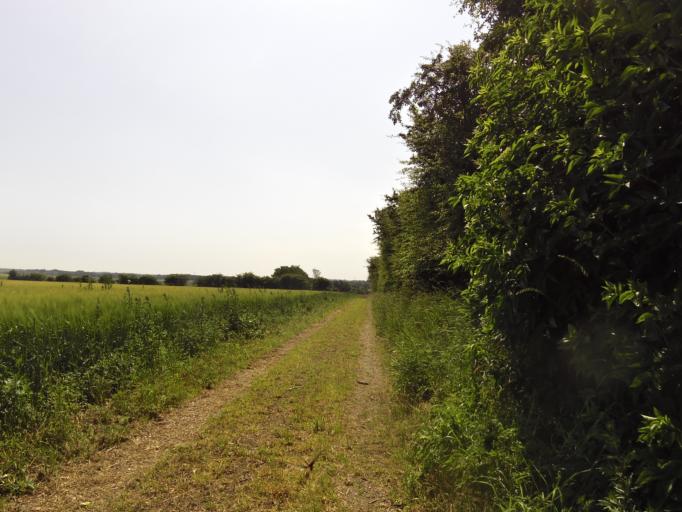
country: DK
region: South Denmark
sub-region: Aabenraa Kommune
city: Rodekro
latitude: 55.1473
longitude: 9.2455
